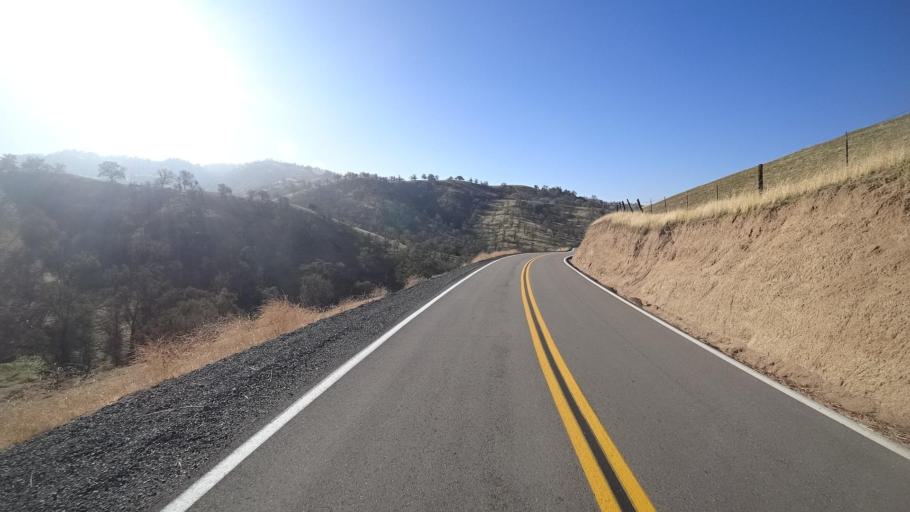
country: US
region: California
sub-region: Kern County
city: Alta Sierra
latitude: 35.7162
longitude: -118.8112
